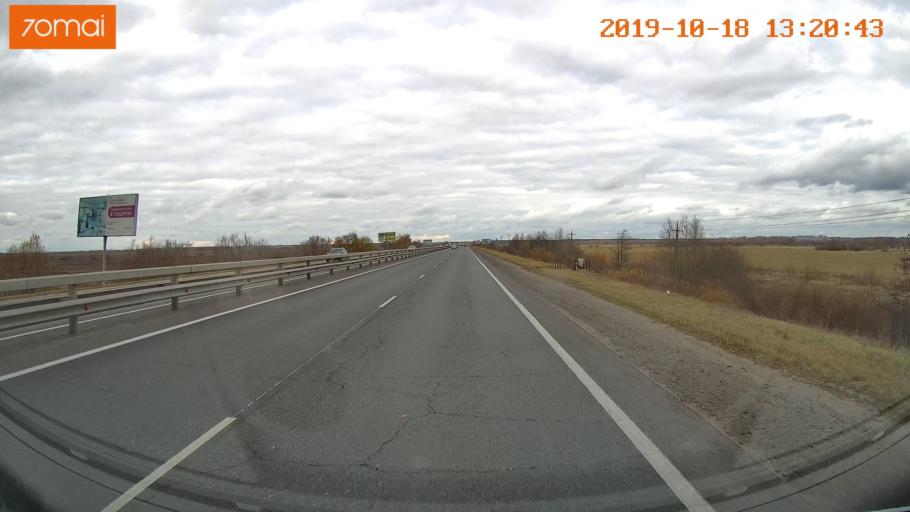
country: RU
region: Rjazan
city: Polyany
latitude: 54.6849
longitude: 39.8340
